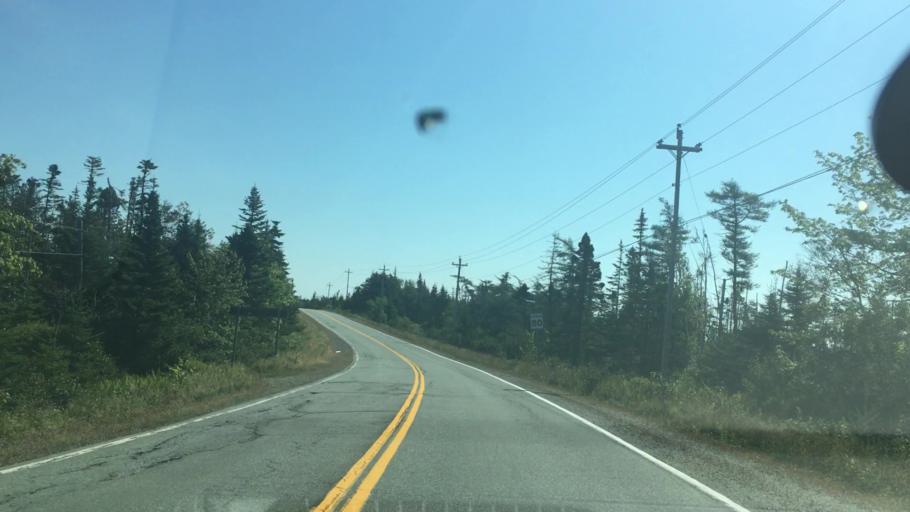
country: CA
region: Nova Scotia
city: New Glasgow
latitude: 44.9182
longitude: -62.3328
